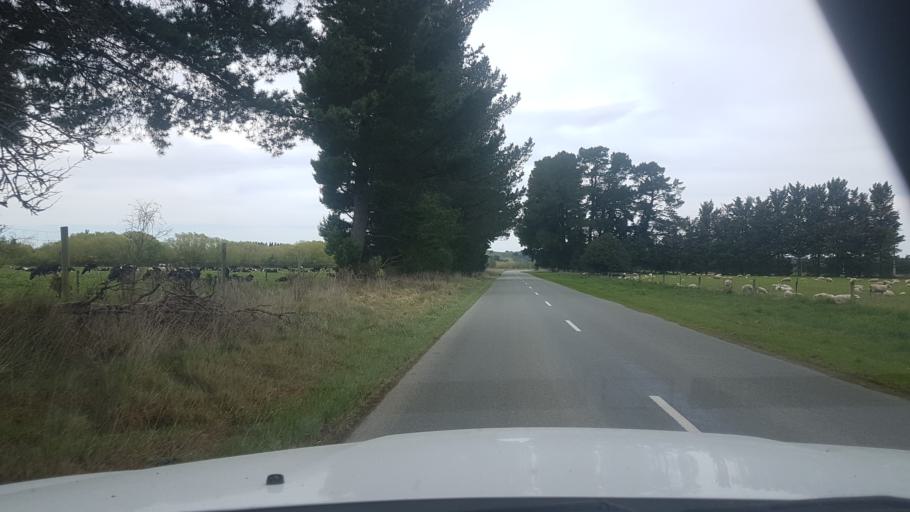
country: NZ
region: Canterbury
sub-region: Timaru District
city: Pleasant Point
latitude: -44.0723
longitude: 171.1609
